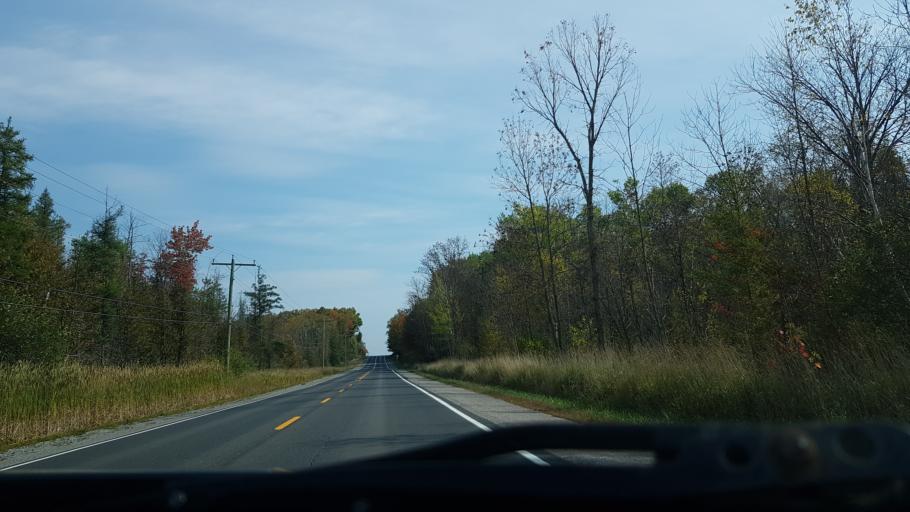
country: CA
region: Ontario
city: Orillia
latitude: 44.6387
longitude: -79.1736
